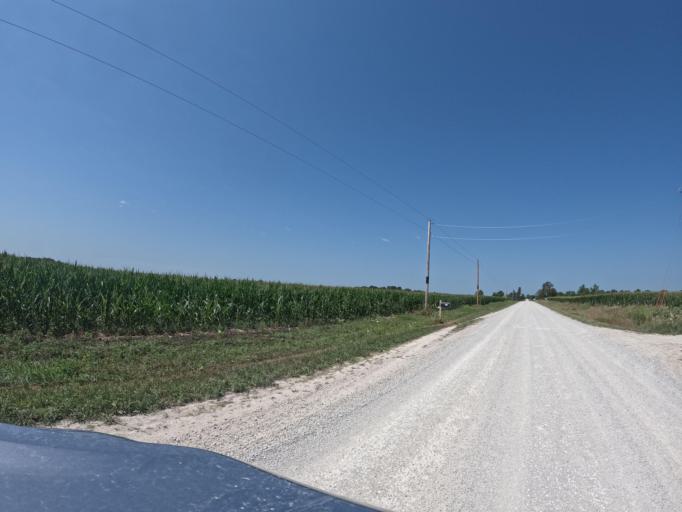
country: US
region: Iowa
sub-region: Henry County
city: Mount Pleasant
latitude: 40.8892
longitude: -91.5786
